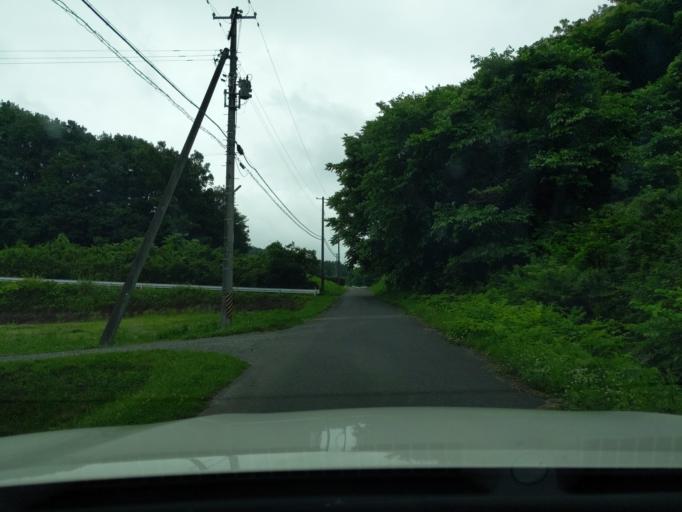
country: JP
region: Fukushima
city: Miharu
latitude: 37.4065
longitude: 140.4400
